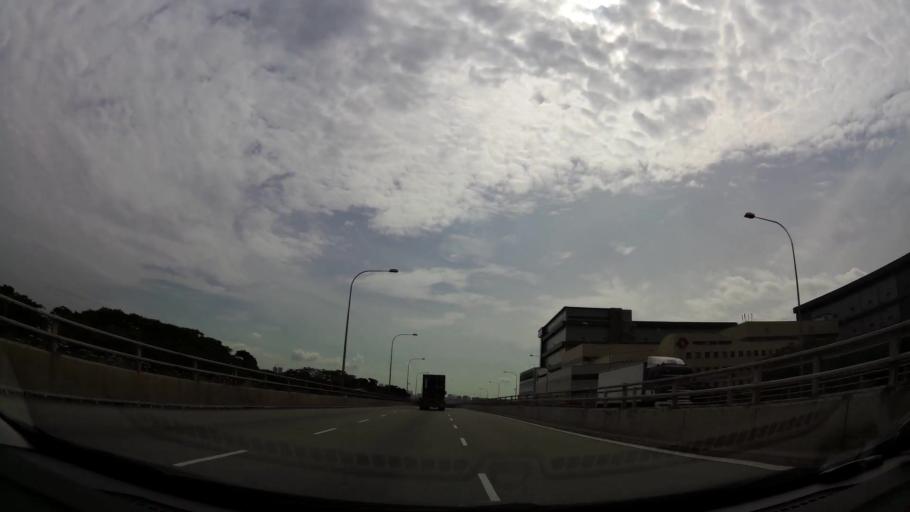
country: SG
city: Singapore
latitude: 1.3114
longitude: 103.7341
